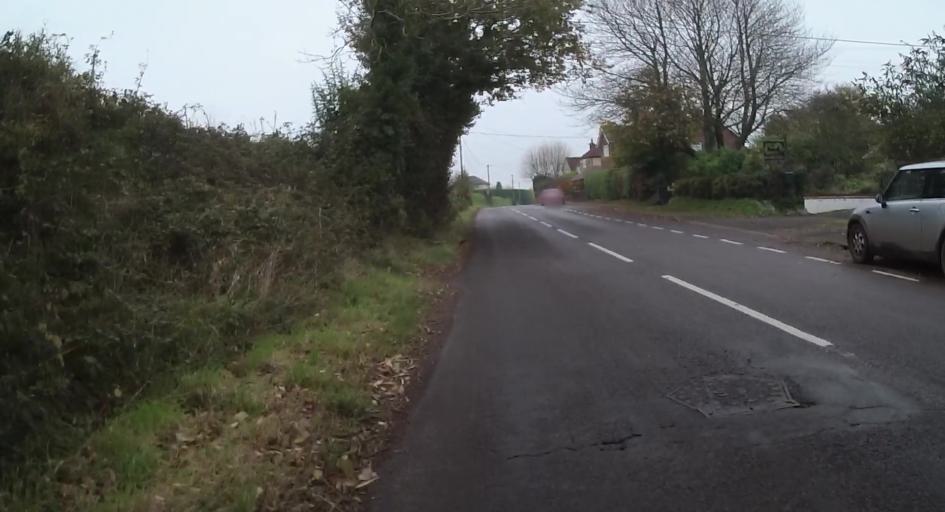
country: GB
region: England
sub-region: Hampshire
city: Kingsley
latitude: 51.1646
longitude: -0.8884
